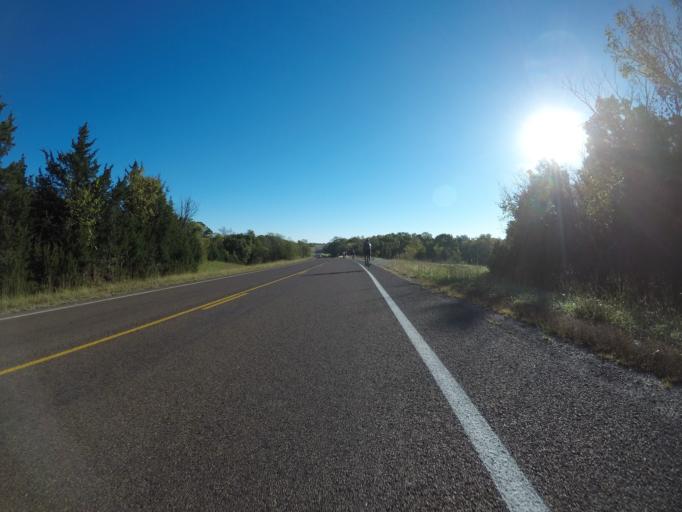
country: US
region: Kansas
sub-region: Douglas County
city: Eudora
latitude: 39.0007
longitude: -95.1443
